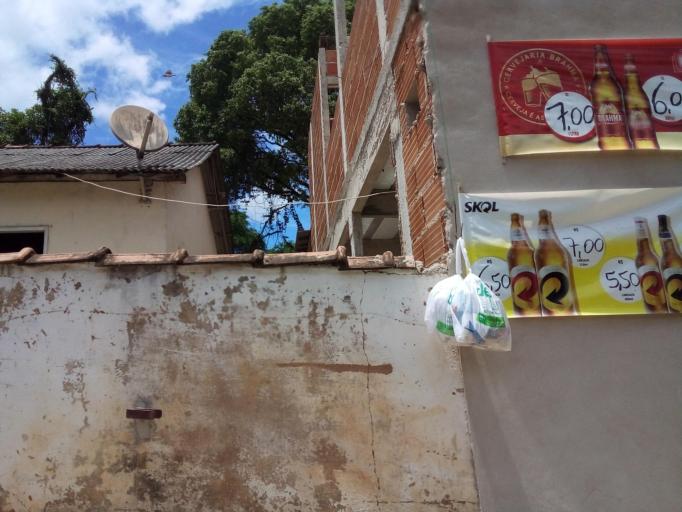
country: BR
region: Espirito Santo
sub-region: Fundao
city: Fundao
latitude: -19.9320
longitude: -40.4017
